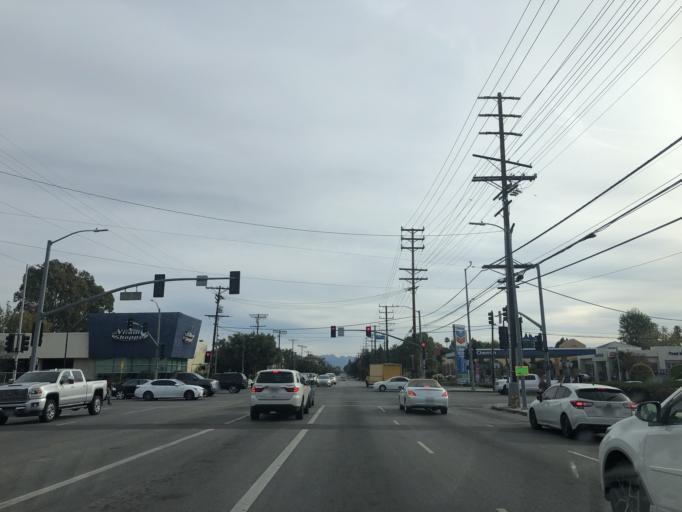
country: US
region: California
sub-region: Los Angeles County
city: Northridge
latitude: 34.2353
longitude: -118.5543
